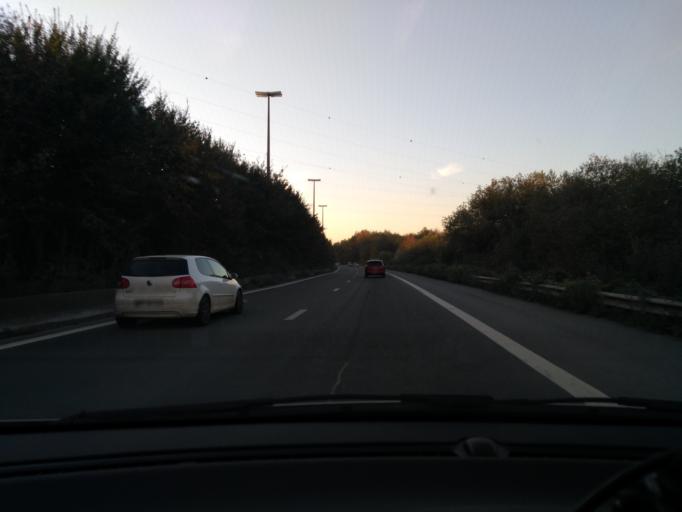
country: BE
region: Wallonia
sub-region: Province du Hainaut
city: Antoing
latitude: 50.5915
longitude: 3.4699
